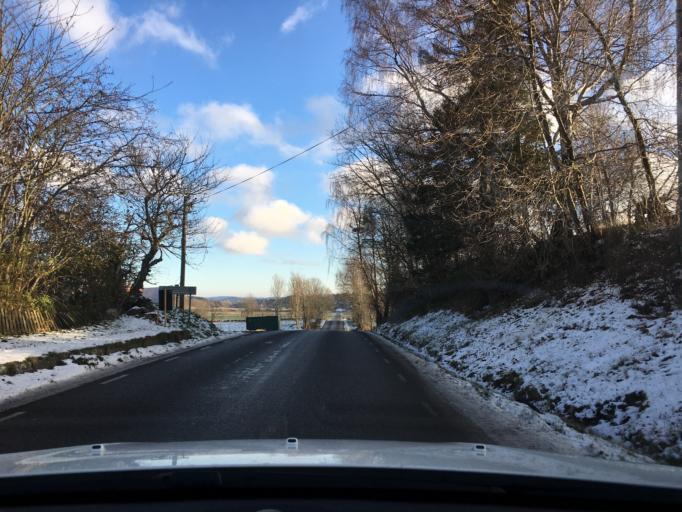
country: SE
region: Vaestra Goetaland
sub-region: Tjorns Kommun
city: Myggenas
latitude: 58.0507
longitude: 11.7115
